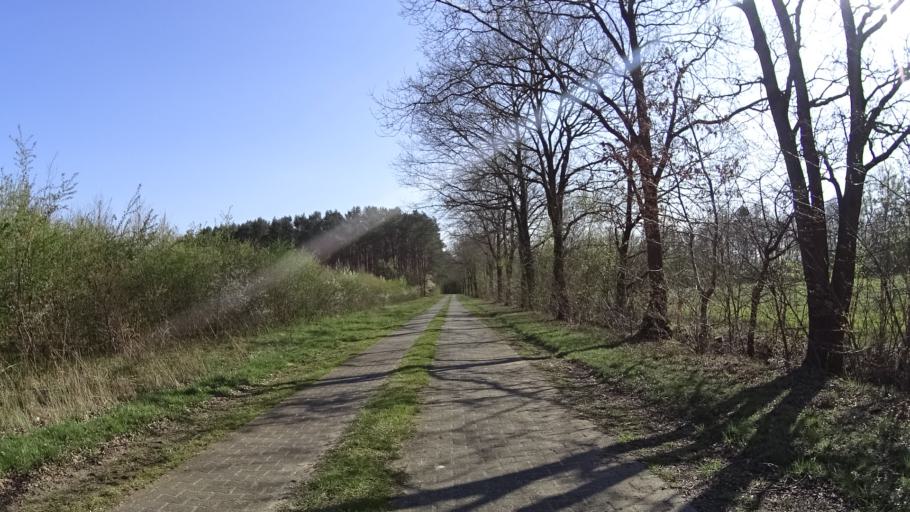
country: DE
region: Lower Saxony
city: Lehe
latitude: 52.9912
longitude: 7.3229
